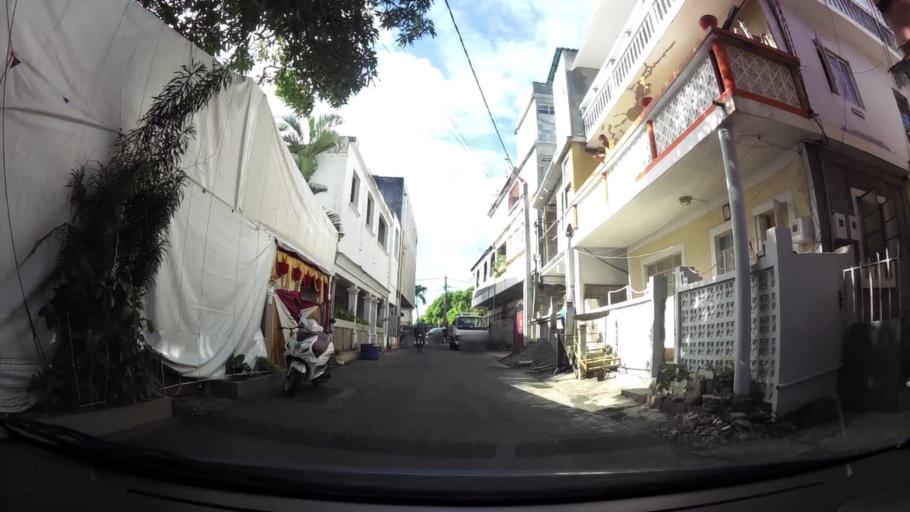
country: MU
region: Grand Port
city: Mahebourg
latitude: -20.4114
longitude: 57.7055
